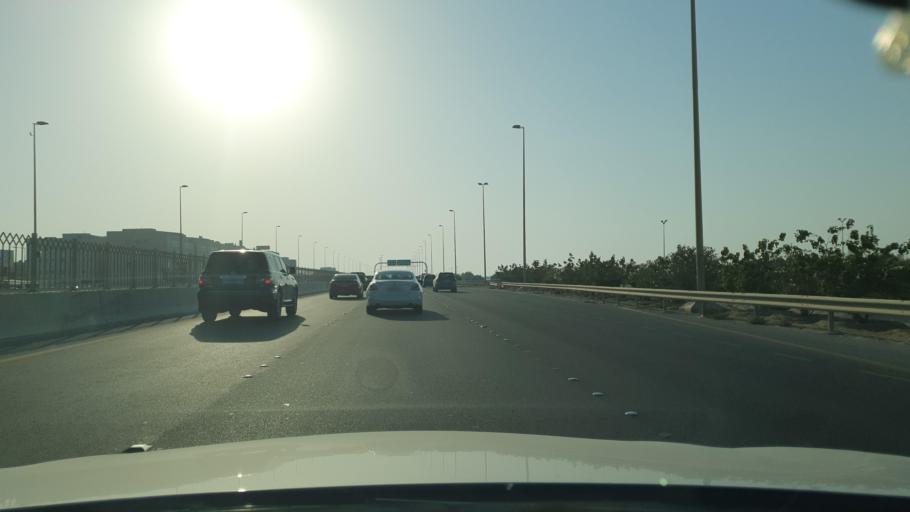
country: BH
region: Muharraq
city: Al Hadd
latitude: 26.2808
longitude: 50.6514
